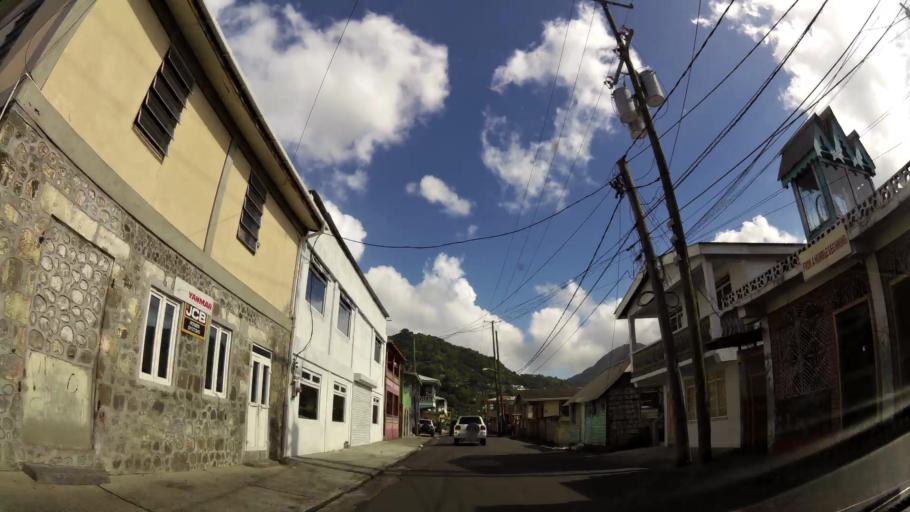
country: DM
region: Saint George
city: Roseau
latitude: 15.2936
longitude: -61.3826
